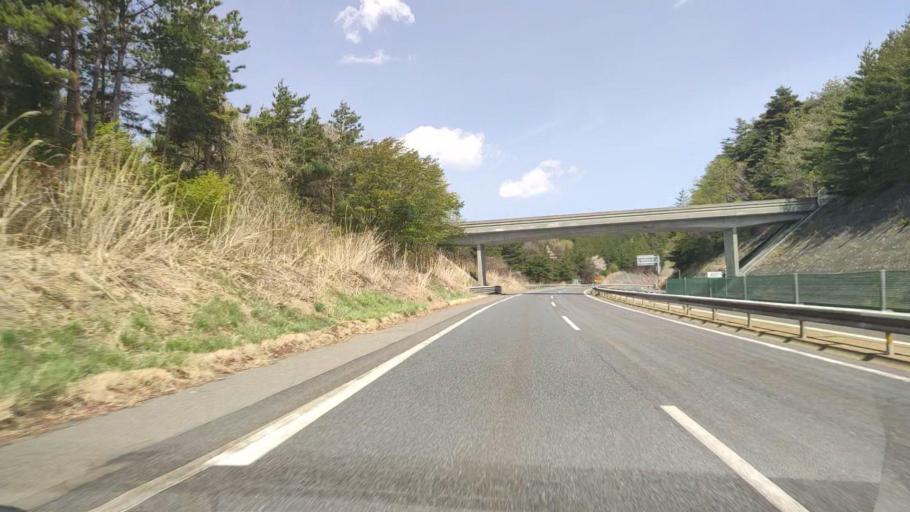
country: JP
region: Iwate
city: Ichinohe
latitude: 40.3008
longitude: 141.4231
